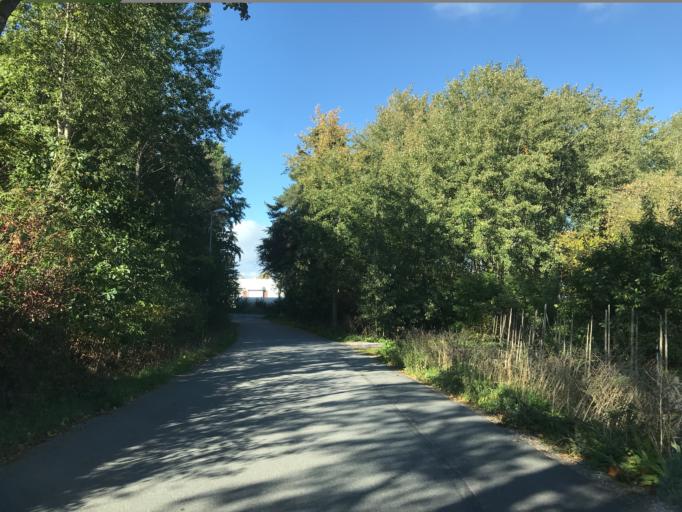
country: SE
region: Stockholm
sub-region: Sollentuna Kommun
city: Sollentuna
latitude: 59.4315
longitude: 17.9304
